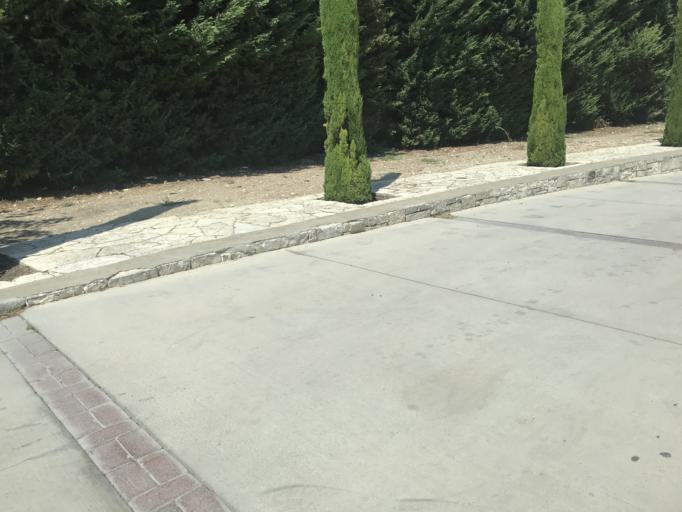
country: TR
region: Izmir
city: Urla
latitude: 38.2528
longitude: 26.7359
